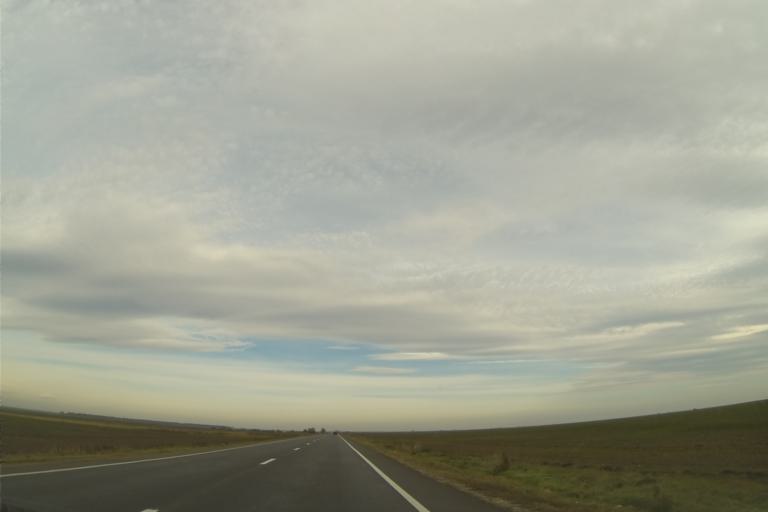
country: RO
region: Olt
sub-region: Comuna Priseaca
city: Priseaca
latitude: 44.5104
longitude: 24.4869
